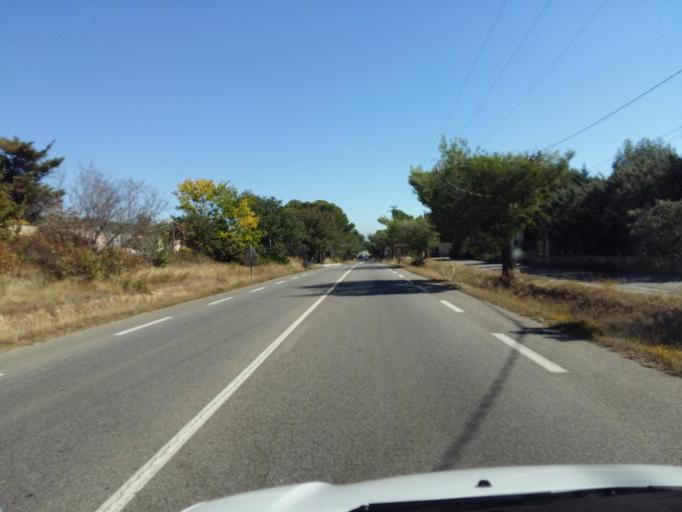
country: FR
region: Provence-Alpes-Cote d'Azur
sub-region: Departement du Vaucluse
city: Merindol
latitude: 43.7532
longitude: 5.1930
